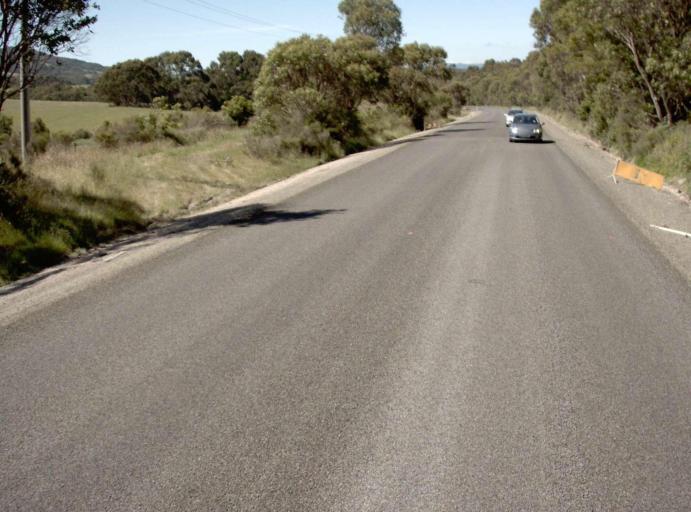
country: AU
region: Victoria
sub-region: Latrobe
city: Morwell
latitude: -38.7386
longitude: 146.1455
